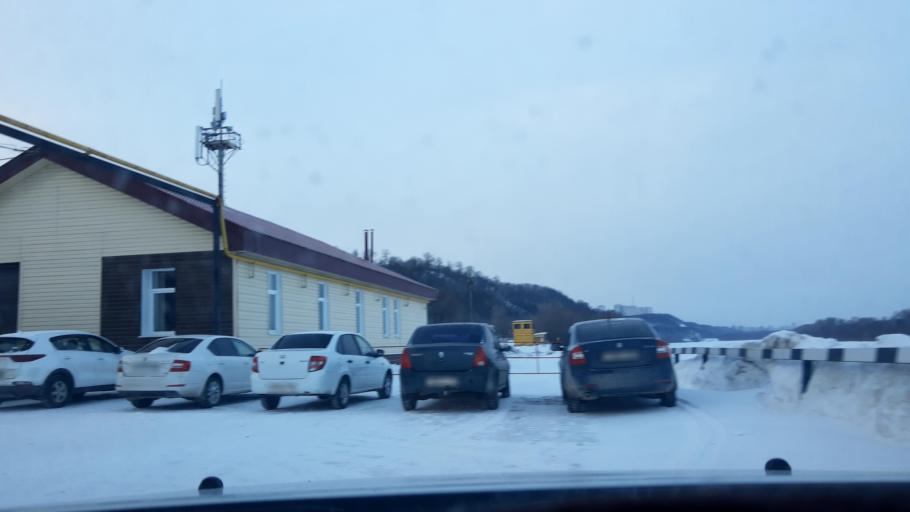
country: RU
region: Bashkortostan
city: Ufa
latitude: 54.8049
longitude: 56.0336
